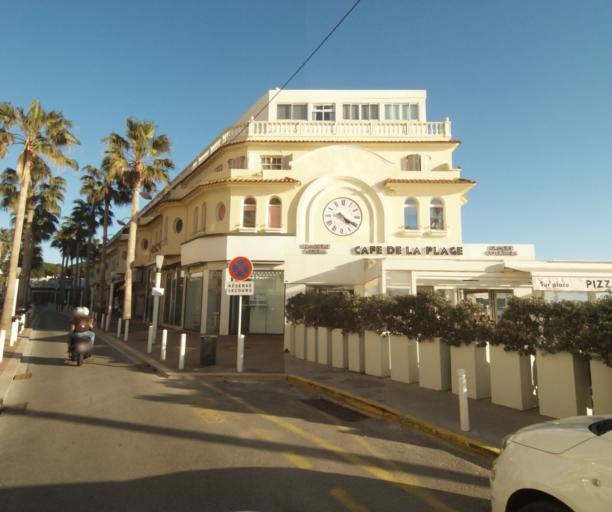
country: FR
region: Provence-Alpes-Cote d'Azur
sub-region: Departement des Alpes-Maritimes
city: Antibes
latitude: 43.5678
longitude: 7.1119
